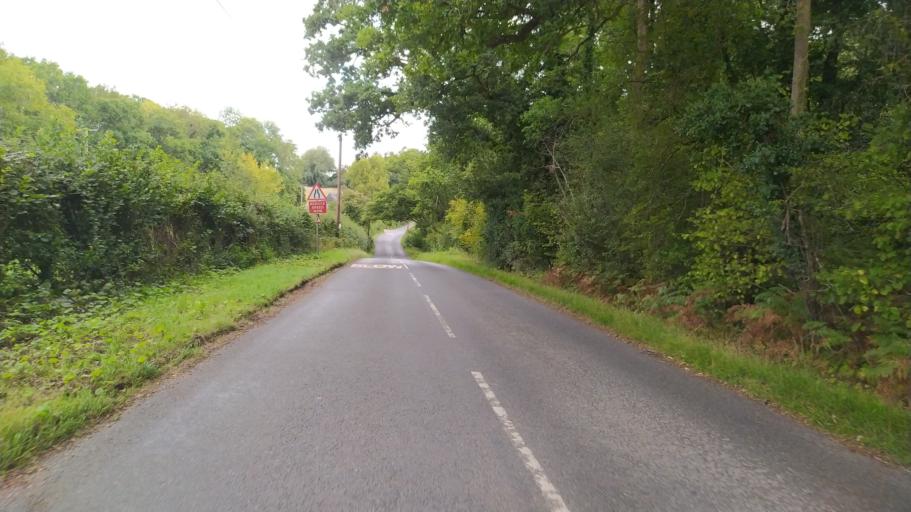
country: GB
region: England
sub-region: Hampshire
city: East Dean
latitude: 51.0480
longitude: -1.5503
